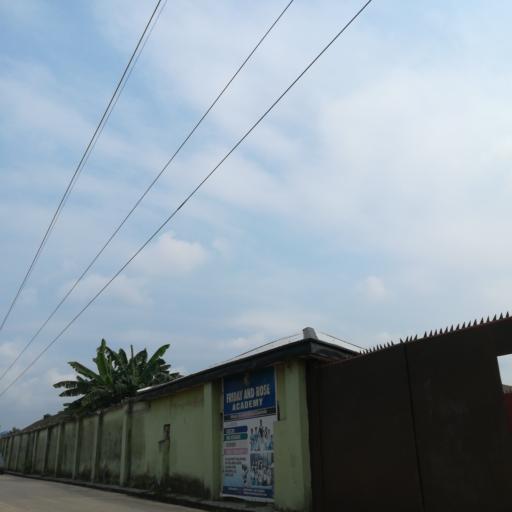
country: NG
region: Rivers
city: Port Harcourt
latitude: 4.8392
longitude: 7.0662
